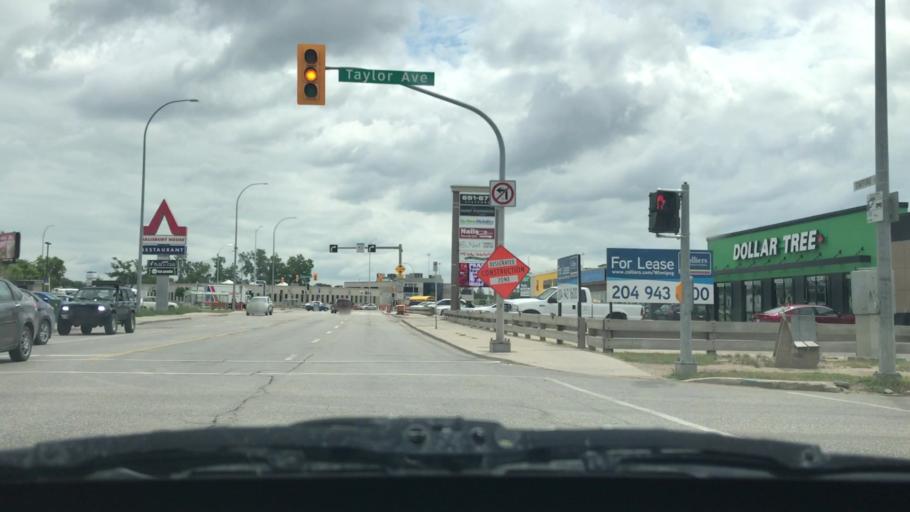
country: CA
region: Manitoba
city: Winnipeg
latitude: 49.8580
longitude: -97.1534
